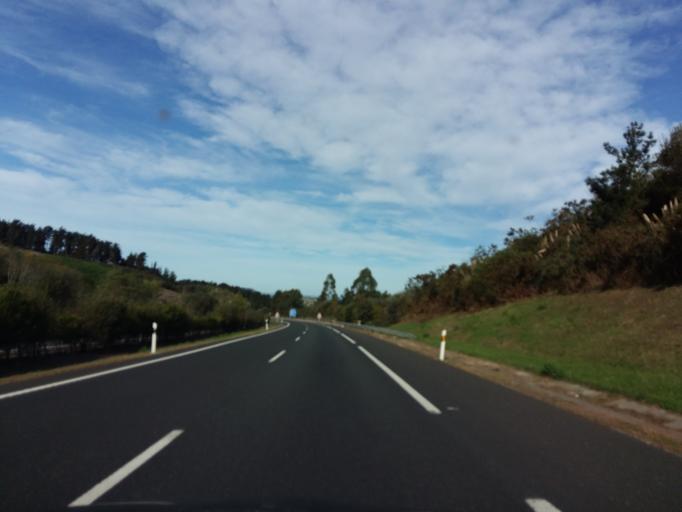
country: ES
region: Cantabria
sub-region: Provincia de Cantabria
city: Comillas
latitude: 43.3313
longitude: -4.3091
